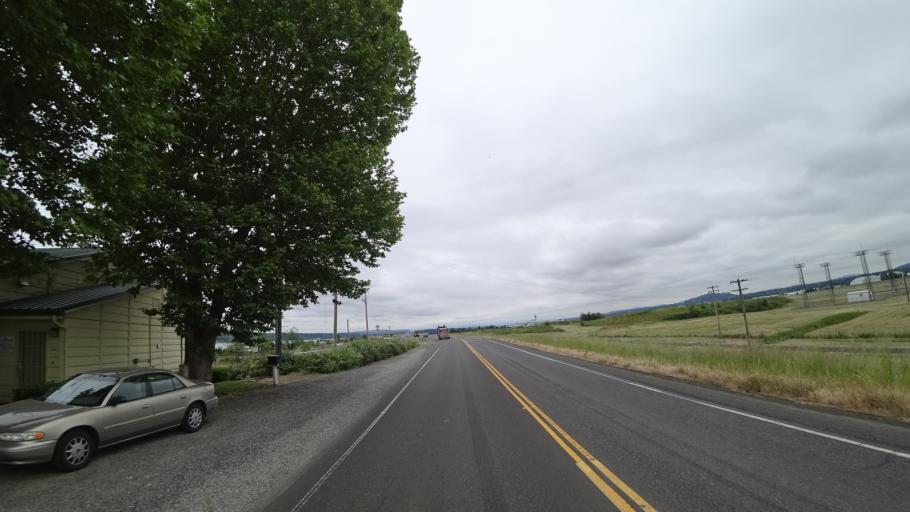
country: US
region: Washington
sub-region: Clark County
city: Vancouver
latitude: 45.6003
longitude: -122.6223
